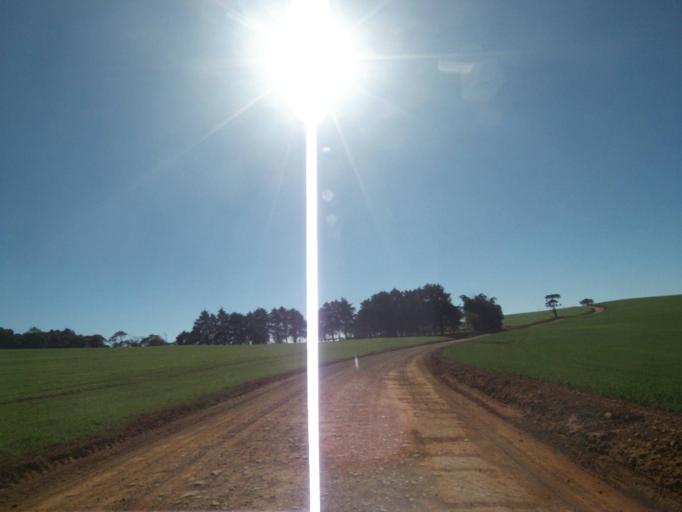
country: BR
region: Parana
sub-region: Tibagi
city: Tibagi
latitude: -24.6095
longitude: -50.6060
